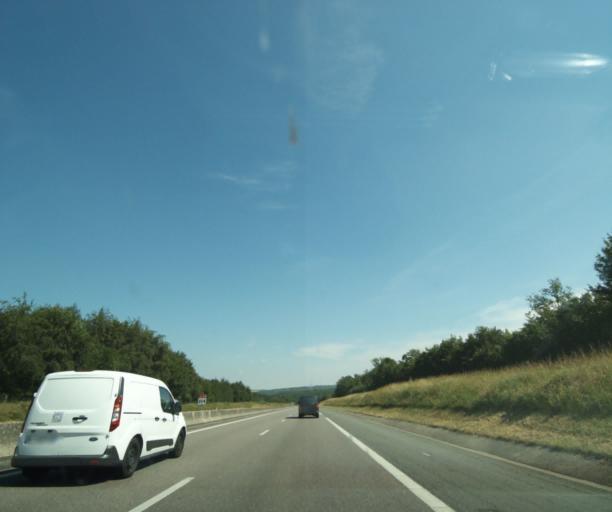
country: FR
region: Lorraine
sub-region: Departement de Meurthe-et-Moselle
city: Colombey-les-Belles
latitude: 48.4499
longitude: 5.8677
